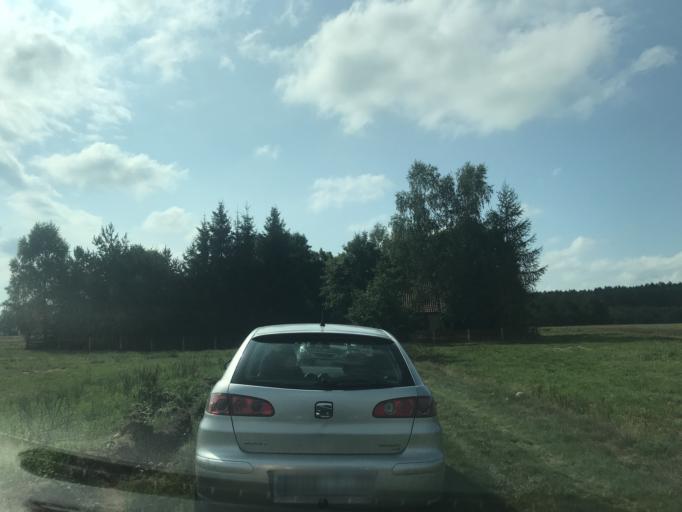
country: PL
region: Warmian-Masurian Voivodeship
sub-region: Powiat nowomiejski
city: Biskupiec
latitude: 53.4202
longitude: 19.4386
